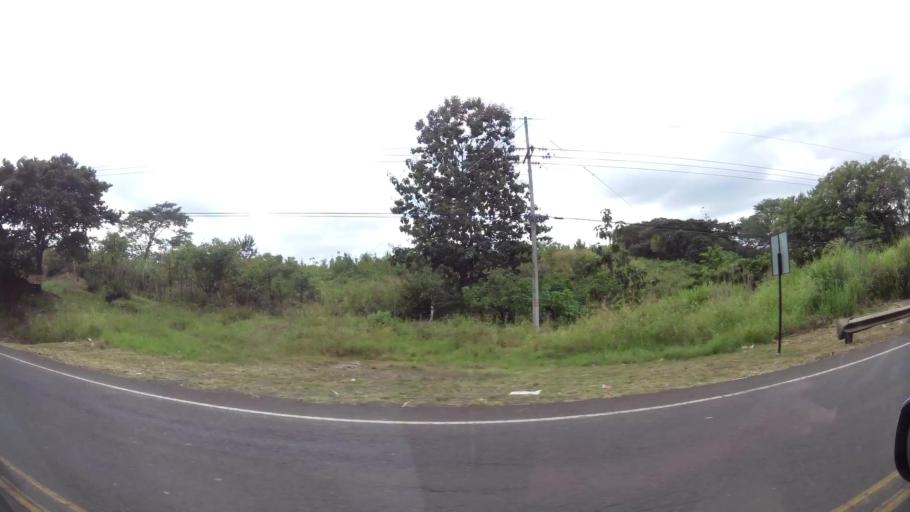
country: CR
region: Alajuela
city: Orotina
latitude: 9.8809
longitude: -84.5760
